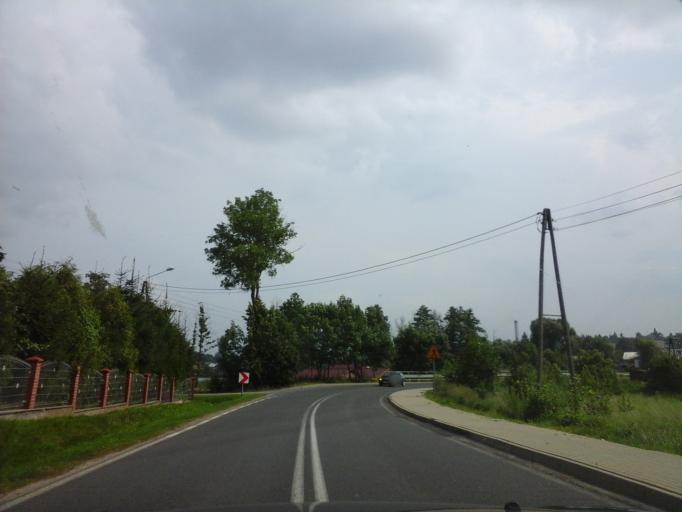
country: PL
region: Lubusz
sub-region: Powiat strzelecko-drezdenecki
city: Dobiegniew
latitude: 52.9756
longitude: 15.7550
